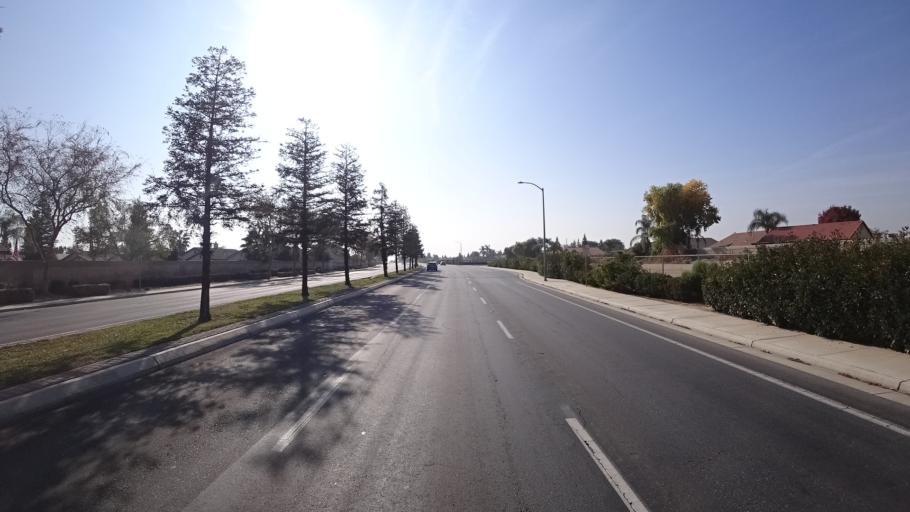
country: US
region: California
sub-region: Kern County
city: Greenacres
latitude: 35.3142
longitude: -119.1098
